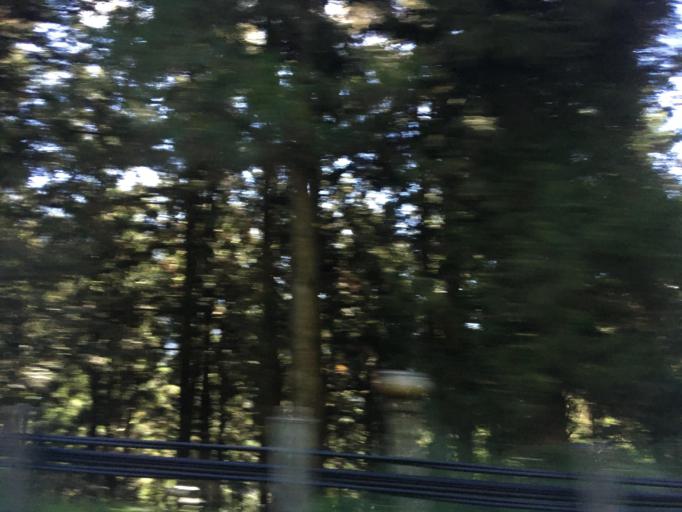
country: TW
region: Taiwan
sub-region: Yilan
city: Yilan
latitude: 24.5011
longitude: 121.5538
